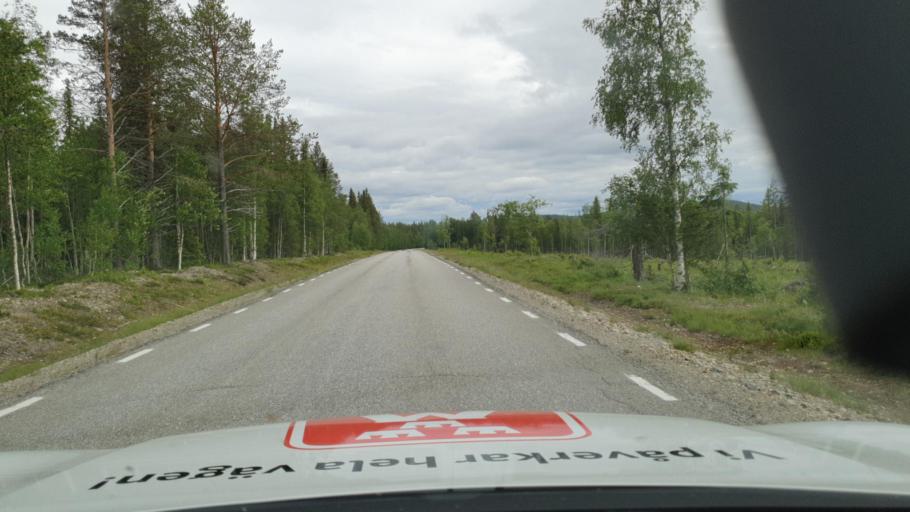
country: SE
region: Vaesterbotten
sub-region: Lycksele Kommun
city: Soderfors
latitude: 64.3395
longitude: 18.1402
